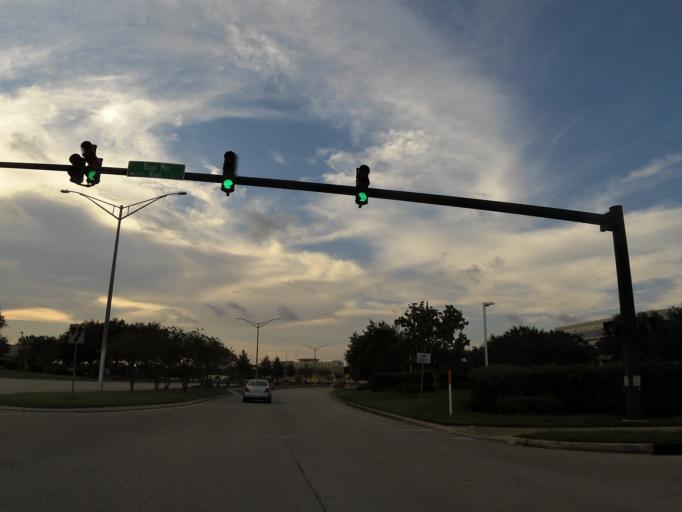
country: US
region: Florida
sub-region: Duval County
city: Jacksonville
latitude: 30.2446
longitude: -81.5349
